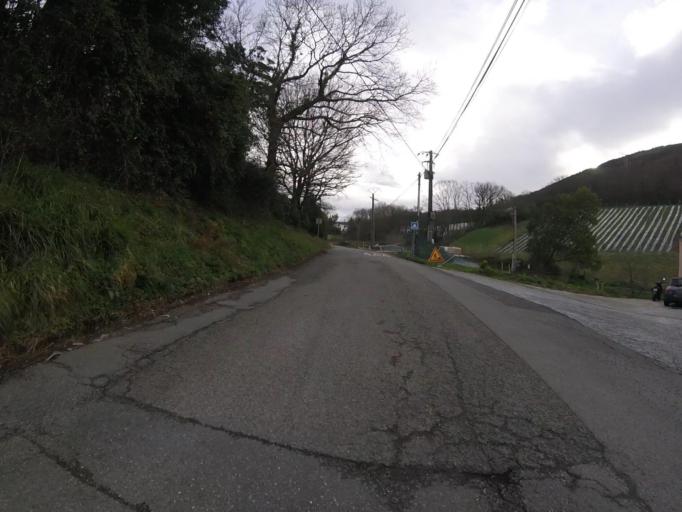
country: FR
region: Aquitaine
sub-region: Departement des Pyrenees-Atlantiques
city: Urrugne
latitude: 43.3422
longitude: -1.7363
